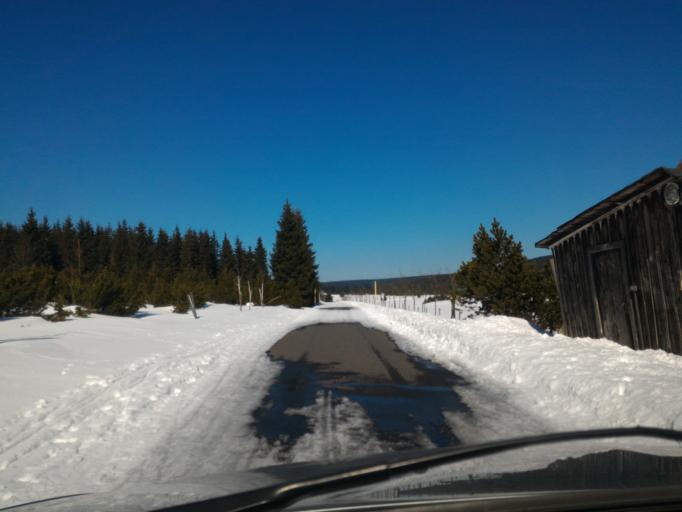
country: CZ
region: Liberecky
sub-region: Okres Jablonec nad Nisou
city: Korenov
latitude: 50.8198
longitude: 15.3433
